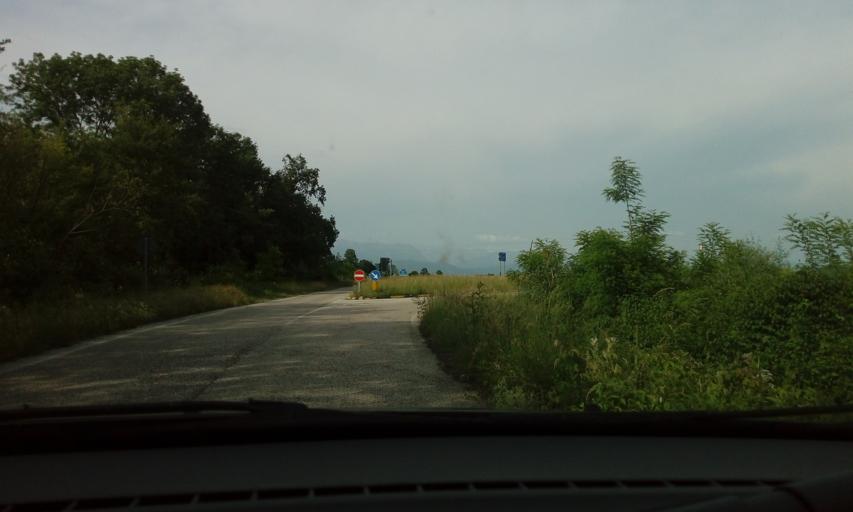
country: IT
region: Friuli Venezia Giulia
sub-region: Provincia di Udine
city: Rive d'Arcano
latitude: 46.1423
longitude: 13.0646
